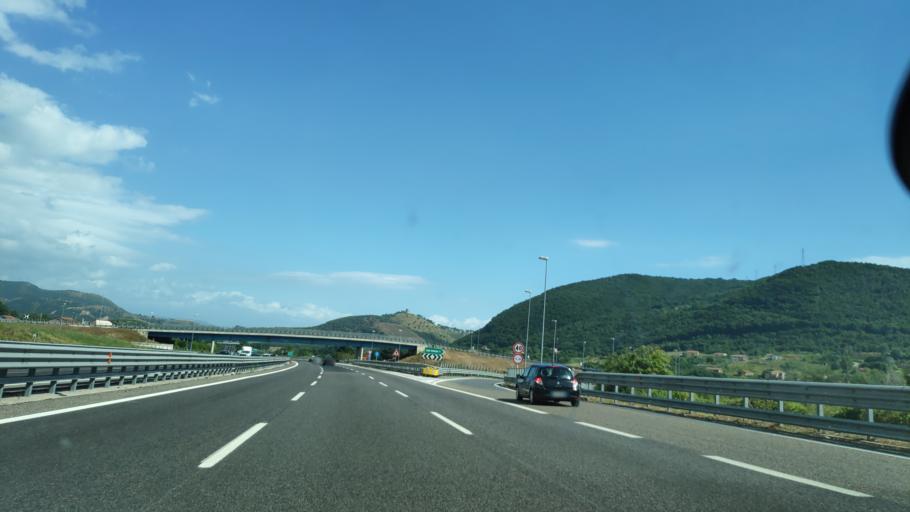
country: IT
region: Campania
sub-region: Provincia di Salerno
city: San Mango Piemonte
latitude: 40.6904
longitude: 14.8374
